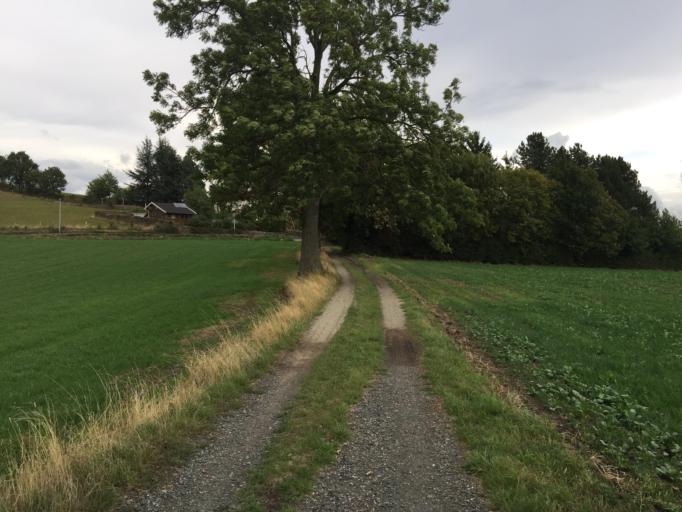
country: FR
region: Rhone-Alpes
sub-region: Departement de la Loire
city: Sorbiers
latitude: 45.4931
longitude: 4.4734
